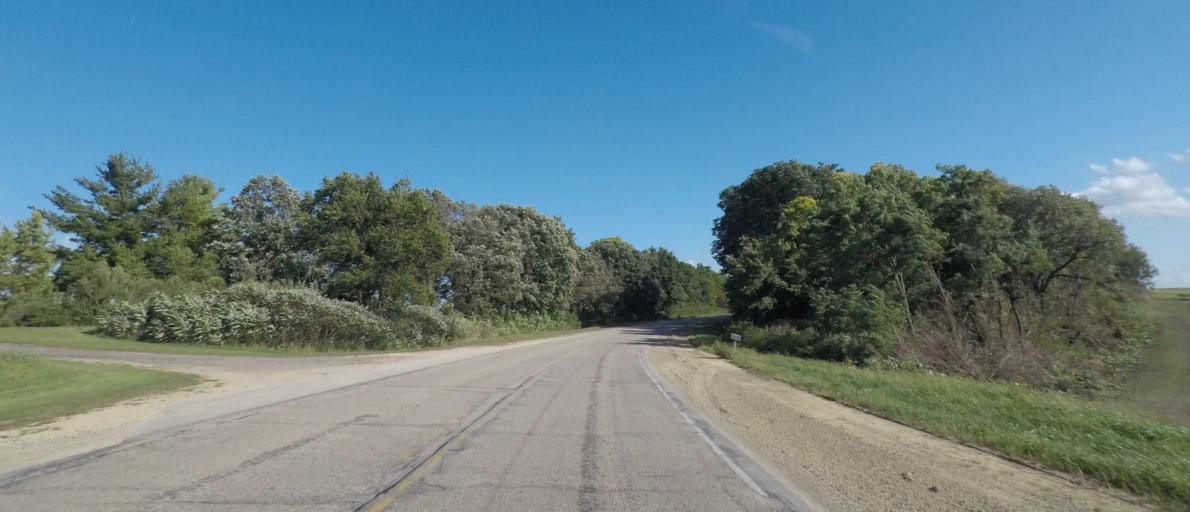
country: US
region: Wisconsin
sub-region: Iowa County
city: Dodgeville
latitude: 42.9758
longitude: -90.0504
